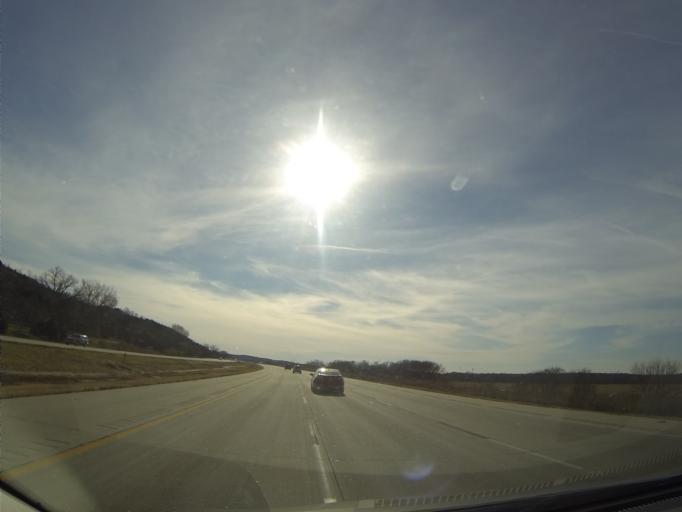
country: US
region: Nebraska
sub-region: Saunders County
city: Ashland
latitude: 41.0518
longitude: -96.2968
